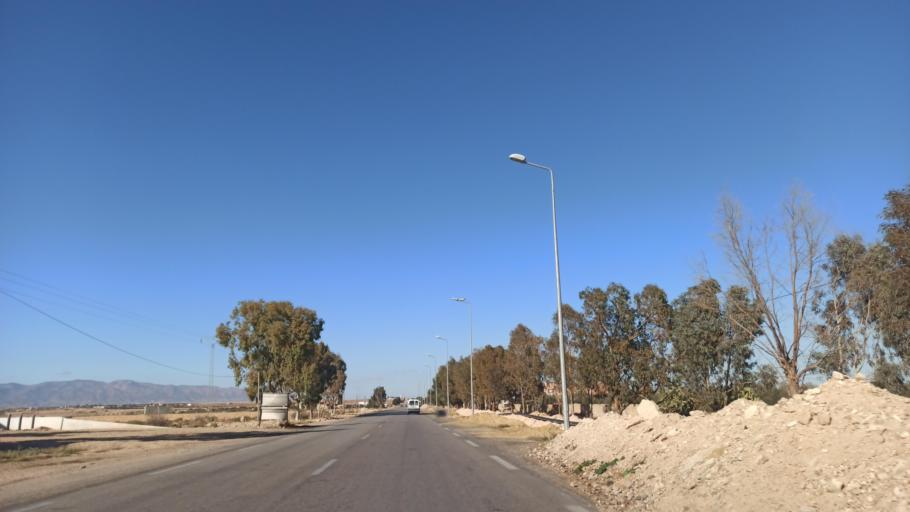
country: TN
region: Sidi Bu Zayd
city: Jilma
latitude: 35.2924
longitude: 9.4172
